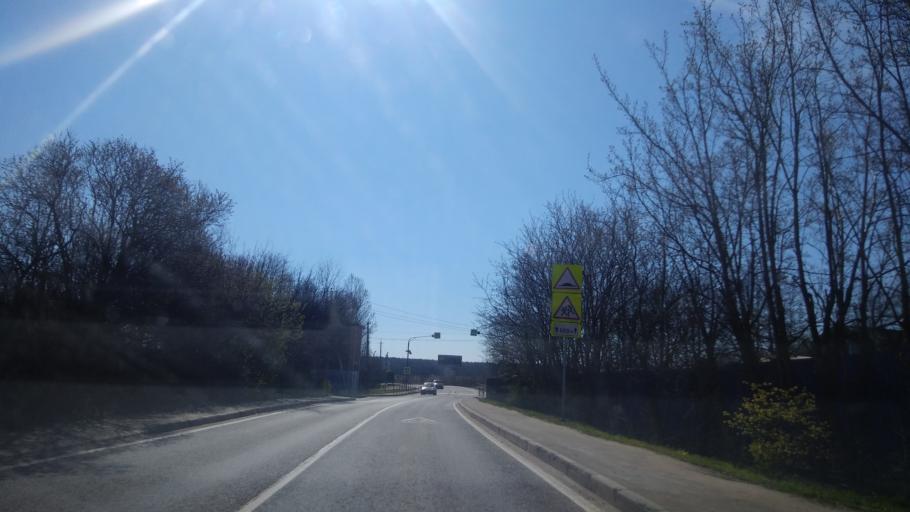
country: RU
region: Moskovskaya
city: Pravdinskiy
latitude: 56.0476
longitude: 37.8780
